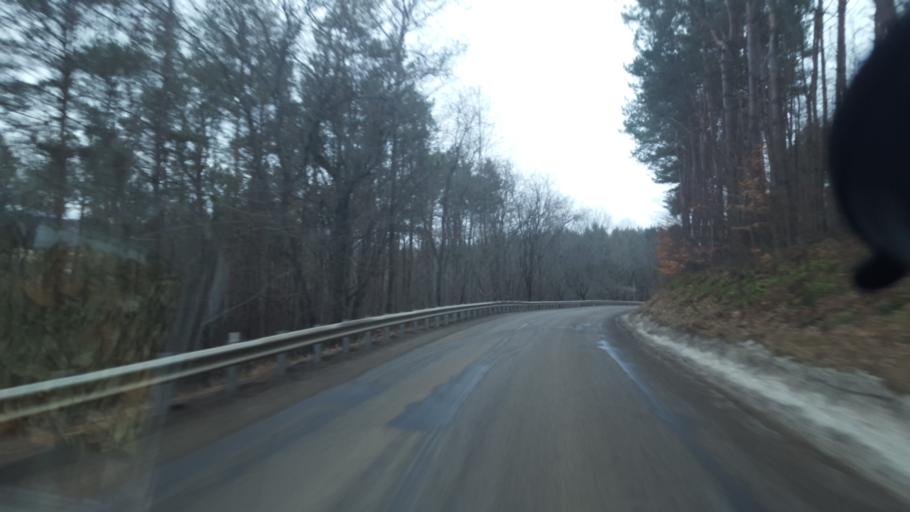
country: US
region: New York
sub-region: Allegany County
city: Wellsville
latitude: 41.9554
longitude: -77.8339
